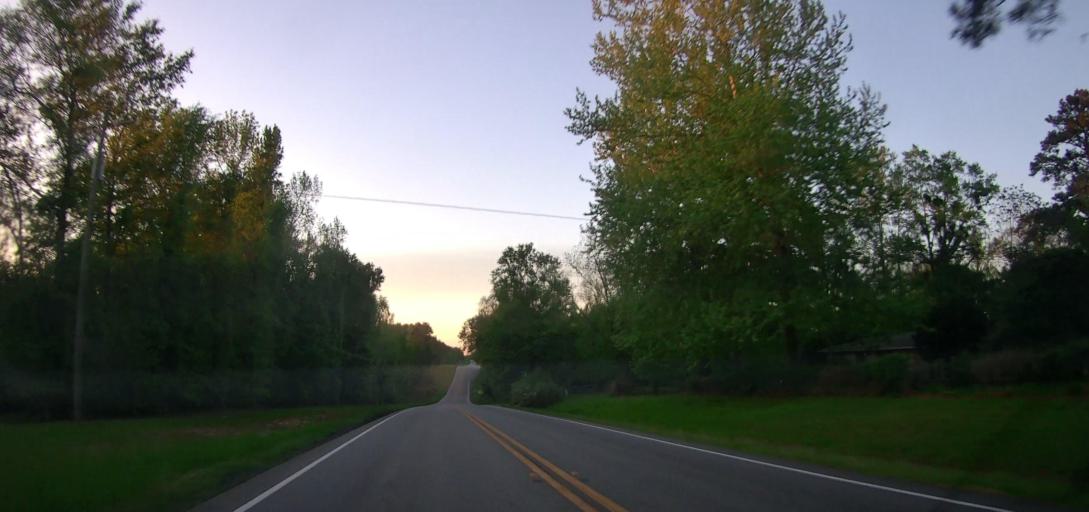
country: US
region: Georgia
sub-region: Marion County
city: Buena Vista
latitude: 32.3575
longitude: -84.5381
